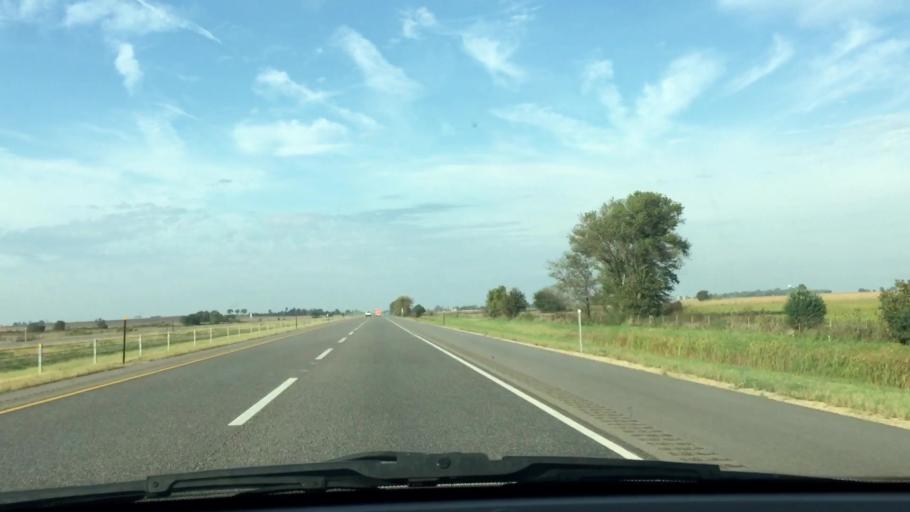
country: US
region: Illinois
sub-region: Ogle County
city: Rochelle
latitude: 41.8679
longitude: -89.1750
